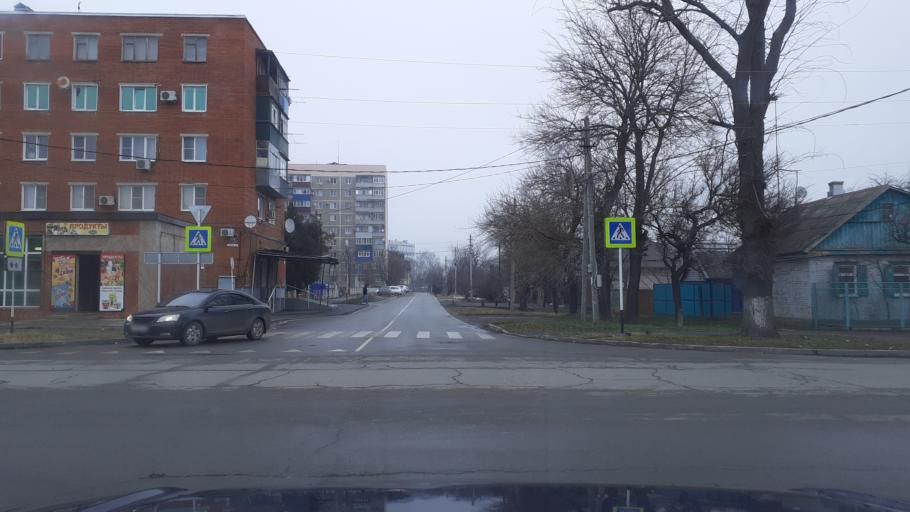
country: RU
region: Adygeya
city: Maykop
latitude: 44.6215
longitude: 40.0701
